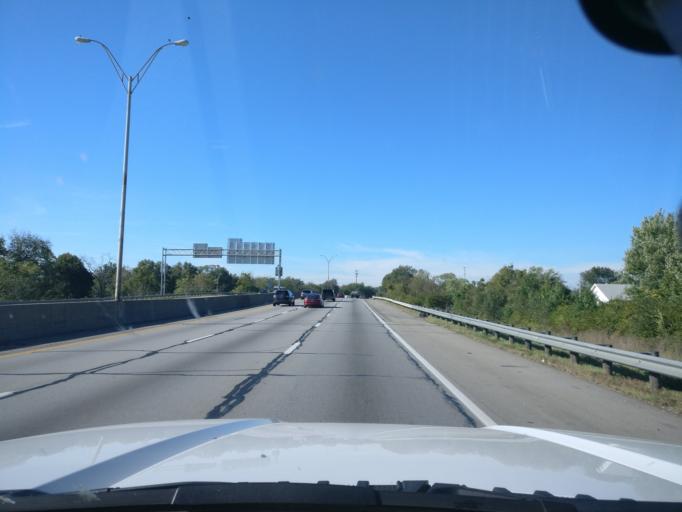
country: US
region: Ohio
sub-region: Montgomery County
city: Northridge
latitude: 39.7936
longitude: -84.1869
